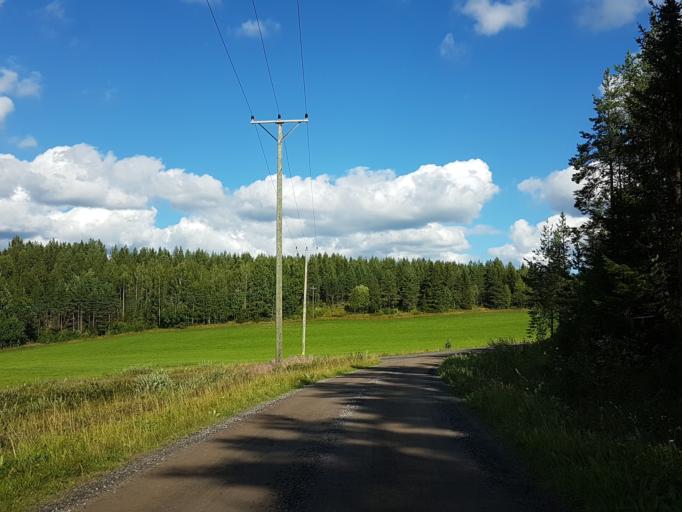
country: SE
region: Vaesterbotten
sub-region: Skelleftea Kommun
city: Burtraesk
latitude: 64.2981
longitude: 20.4885
